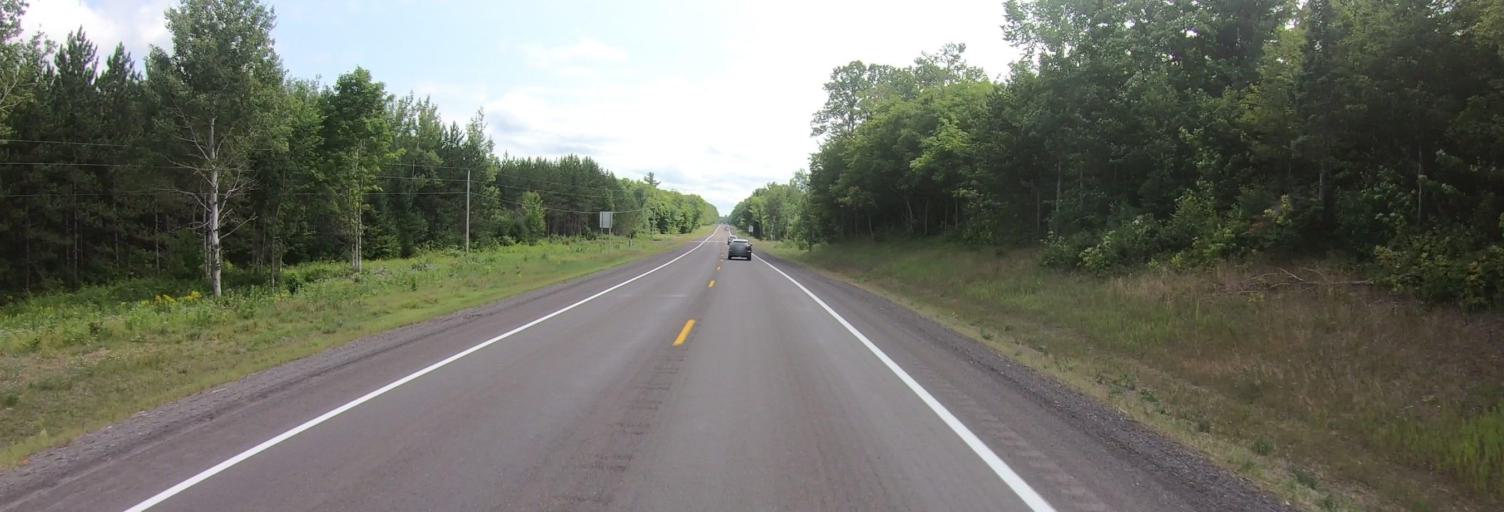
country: US
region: Michigan
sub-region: Houghton County
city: Hancock
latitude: 46.9872
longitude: -88.7813
